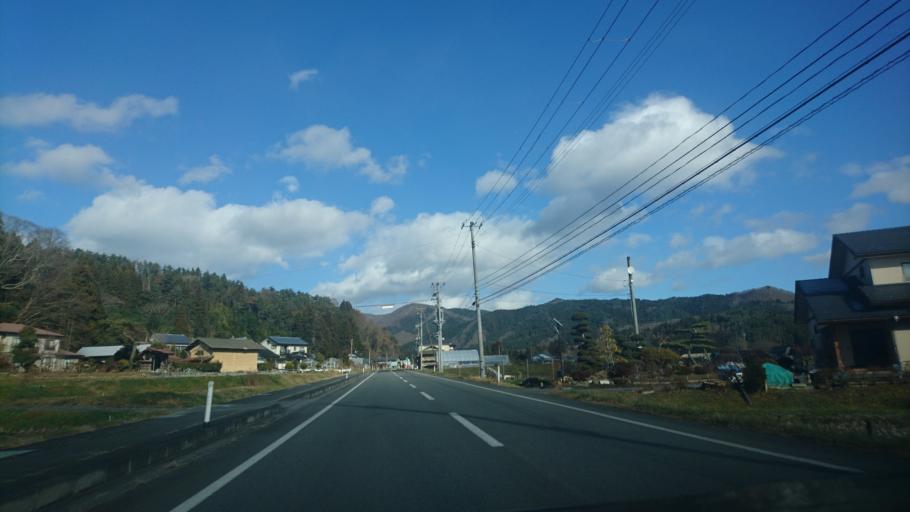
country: JP
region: Iwate
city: Mizusawa
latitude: 39.0639
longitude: 141.3750
